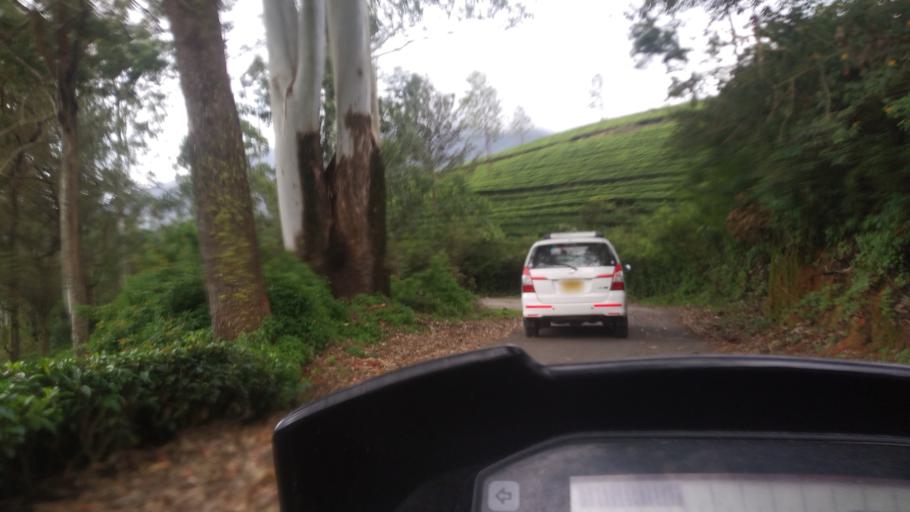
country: IN
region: Kerala
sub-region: Idukki
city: Munnar
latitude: 10.0615
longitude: 77.1069
